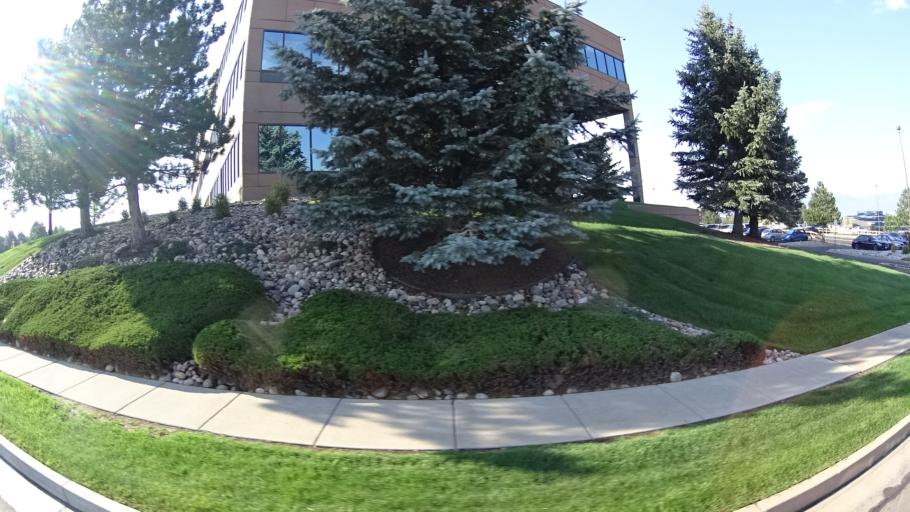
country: US
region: Colorado
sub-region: El Paso County
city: Air Force Academy
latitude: 38.9622
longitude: -104.7937
